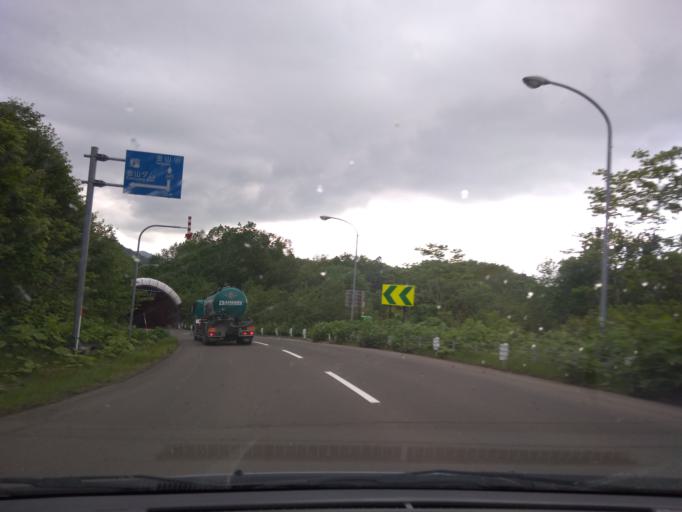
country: JP
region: Hokkaido
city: Shimo-furano
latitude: 43.1333
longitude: 142.4462
